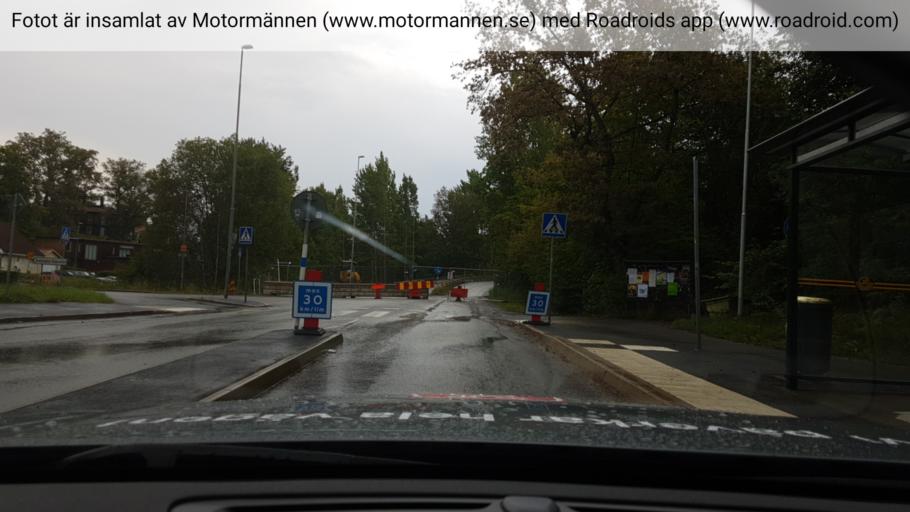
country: SE
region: Stockholm
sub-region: Upplands-Bro Kommun
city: Kungsaengen
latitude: 59.4693
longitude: 17.8004
